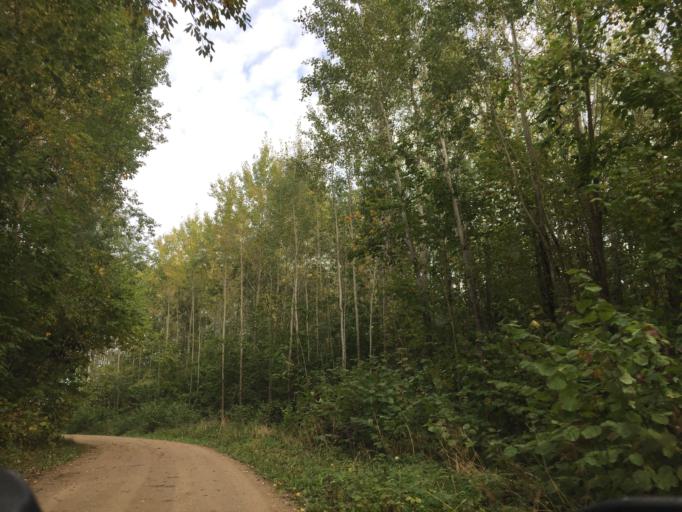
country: LV
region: Jaunpils
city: Jaunpils
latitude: 56.6458
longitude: 23.0796
